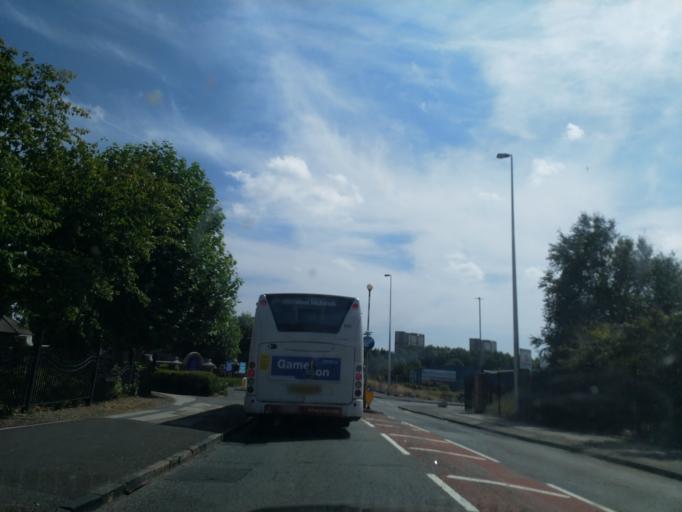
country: GB
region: England
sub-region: City and Borough of Birmingham
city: Birmingham
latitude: 52.4974
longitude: -1.8813
